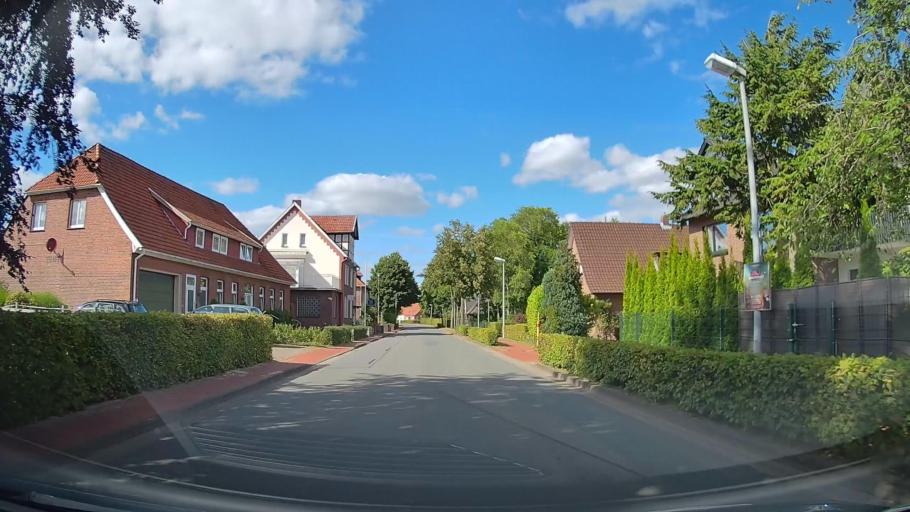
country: DE
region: Lower Saxony
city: Berge
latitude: 52.6175
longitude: 7.7475
